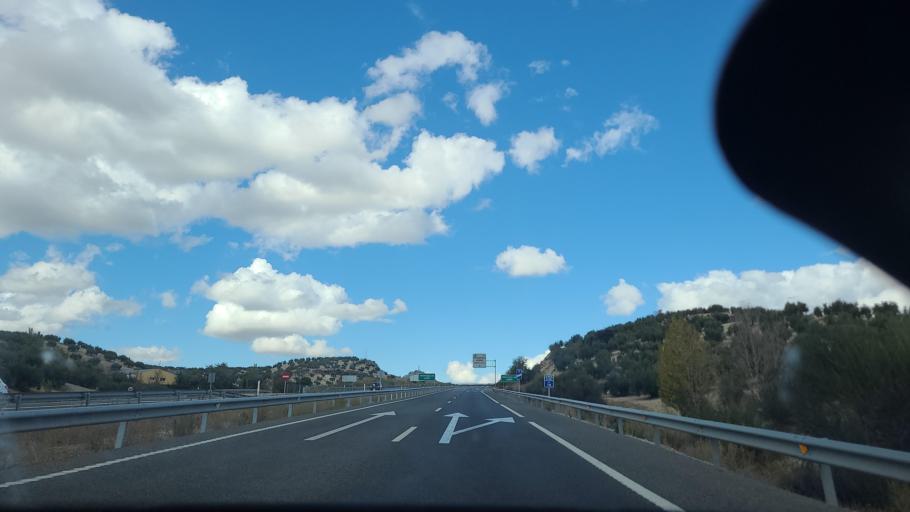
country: ES
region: Andalusia
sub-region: Provincia de Jaen
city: Noalejo
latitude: 37.5256
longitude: -3.6369
